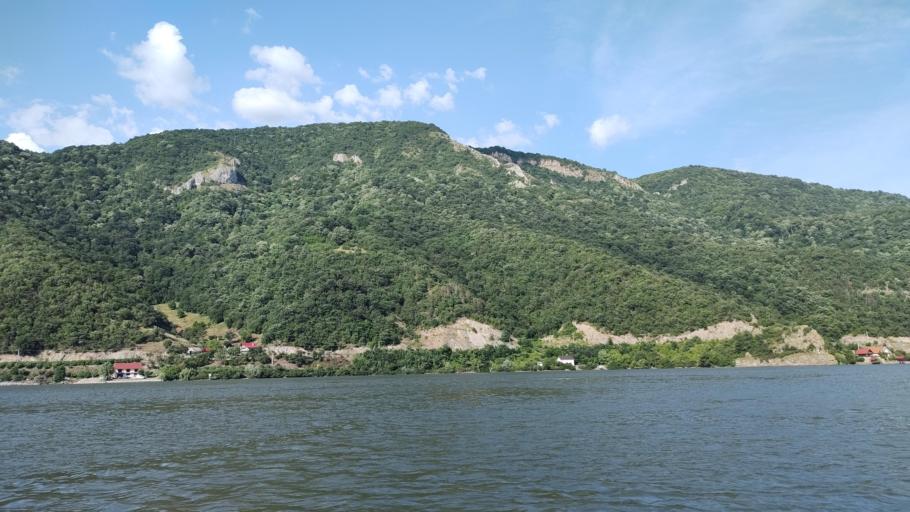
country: RO
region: Caras-Severin
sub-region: Comuna Berzasca
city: Berzasca
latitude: 44.5952
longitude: 22.0218
